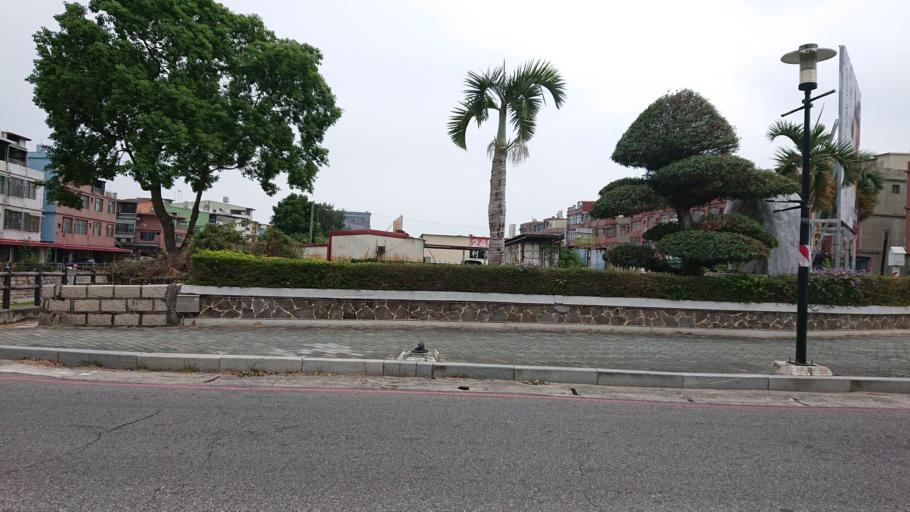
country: TW
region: Fukien
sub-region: Kinmen
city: Jincheng
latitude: 24.4410
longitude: 118.4133
